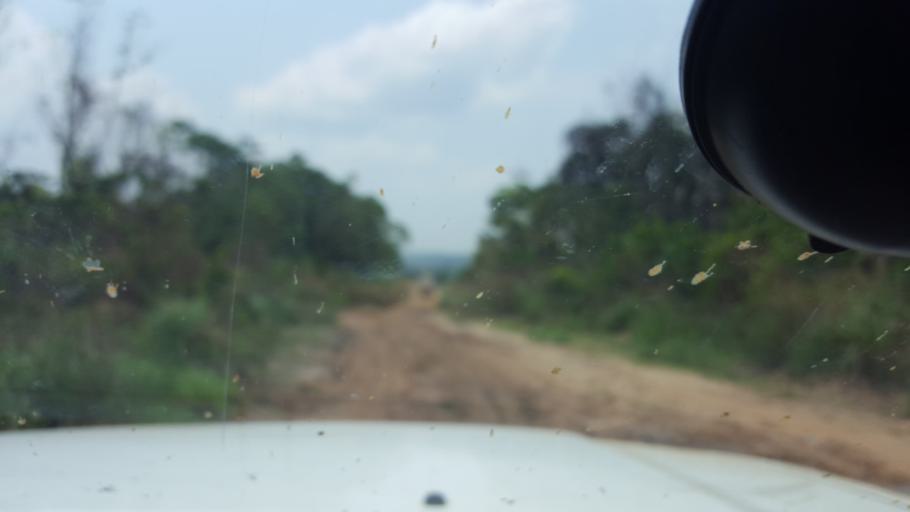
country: CD
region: Bandundu
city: Mushie
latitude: -3.7513
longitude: 16.6382
